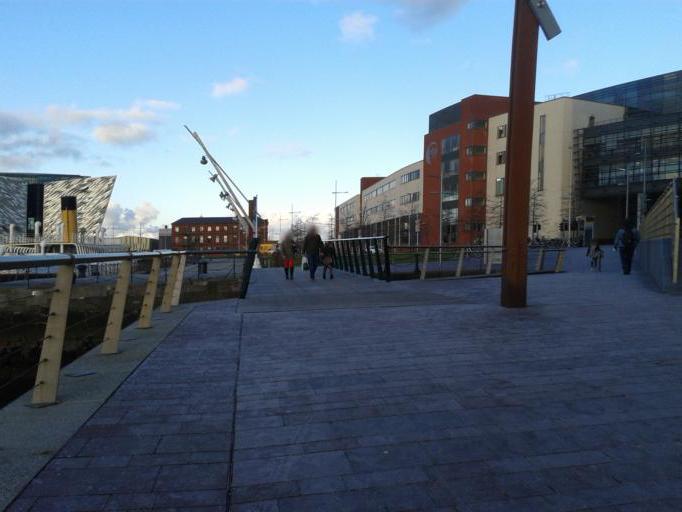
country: GB
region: Northern Ireland
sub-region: City of Belfast
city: Belfast
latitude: 54.6056
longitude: -5.9117
